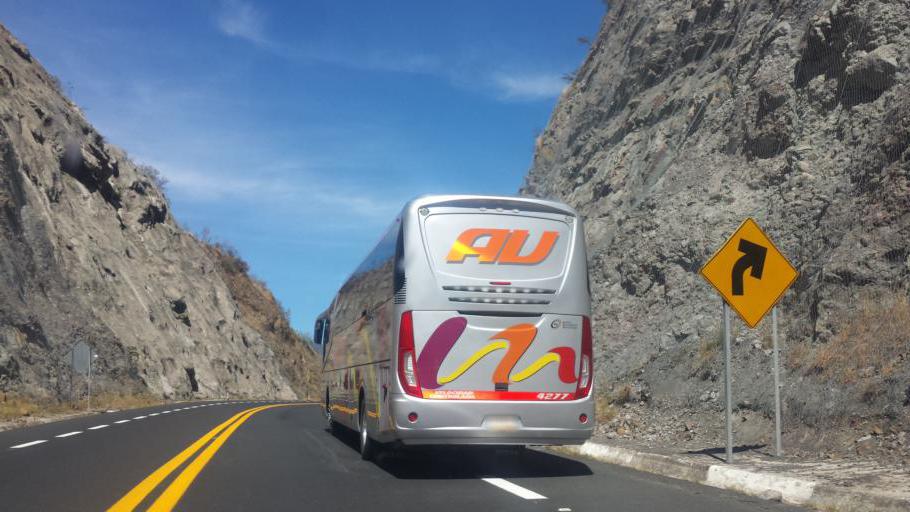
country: MX
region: Puebla
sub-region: San Jose Miahuatlan
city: San Pedro Tetitlan
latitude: 18.0928
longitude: -97.3391
